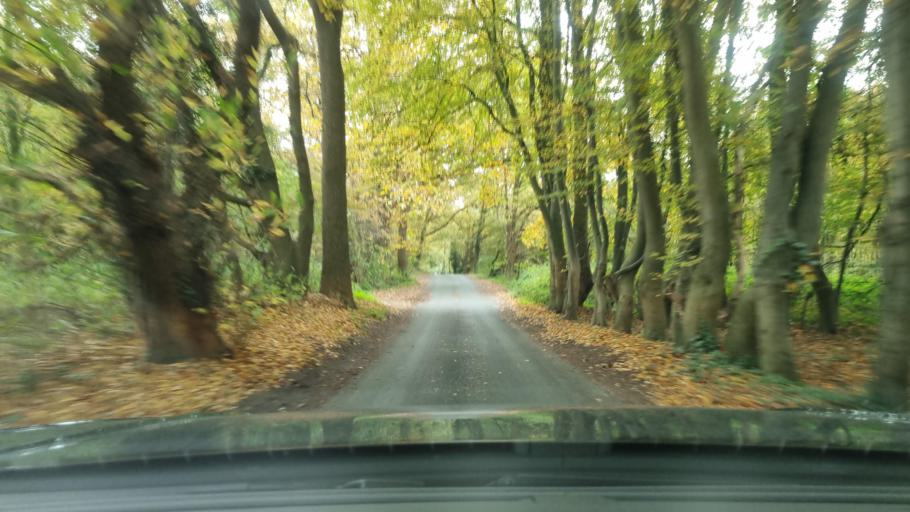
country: DE
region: North Rhine-Westphalia
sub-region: Regierungsbezirk Dusseldorf
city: Kleve
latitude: 51.7915
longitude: 6.1041
